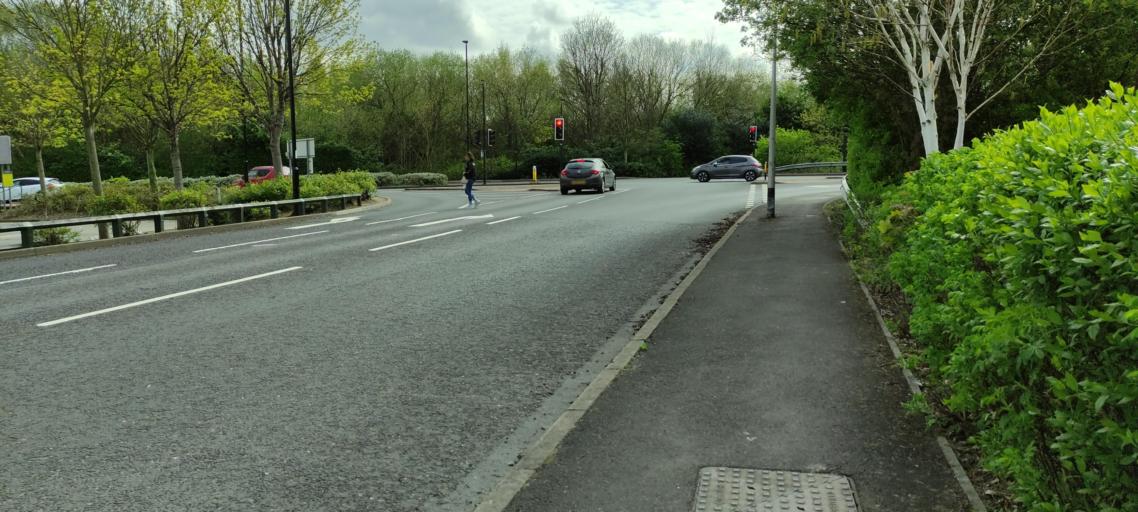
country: GB
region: England
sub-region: Rotherham
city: Wentworth
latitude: 53.4115
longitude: -1.4173
